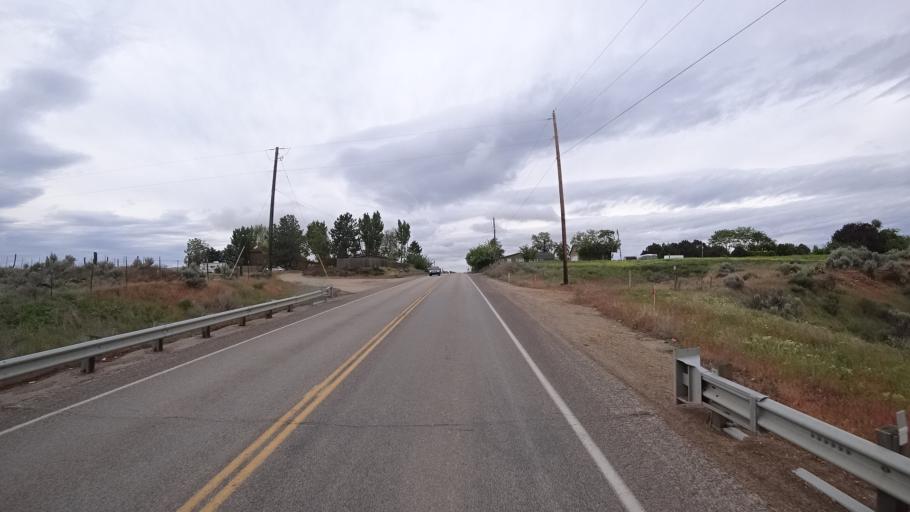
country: US
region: Idaho
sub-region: Ada County
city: Star
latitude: 43.6678
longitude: -116.4934
